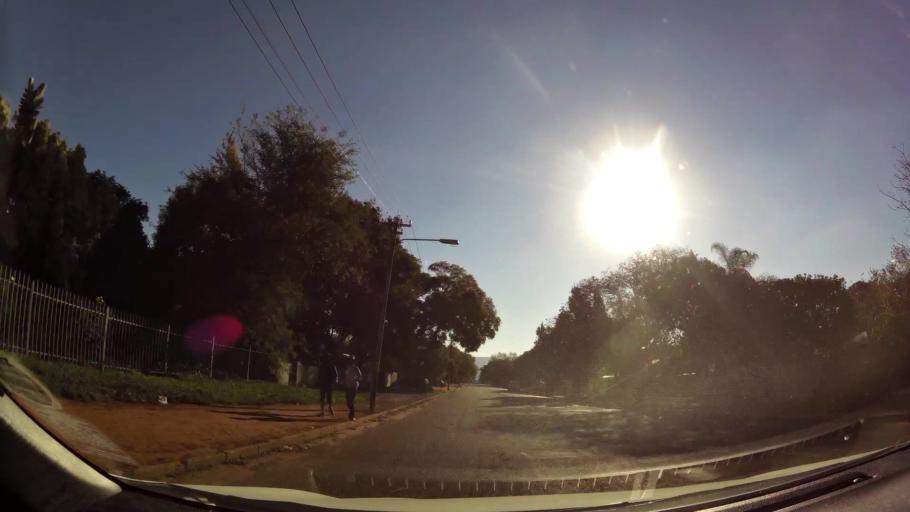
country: ZA
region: Limpopo
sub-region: Waterberg District Municipality
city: Mokopane
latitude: -24.1846
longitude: 29.0070
